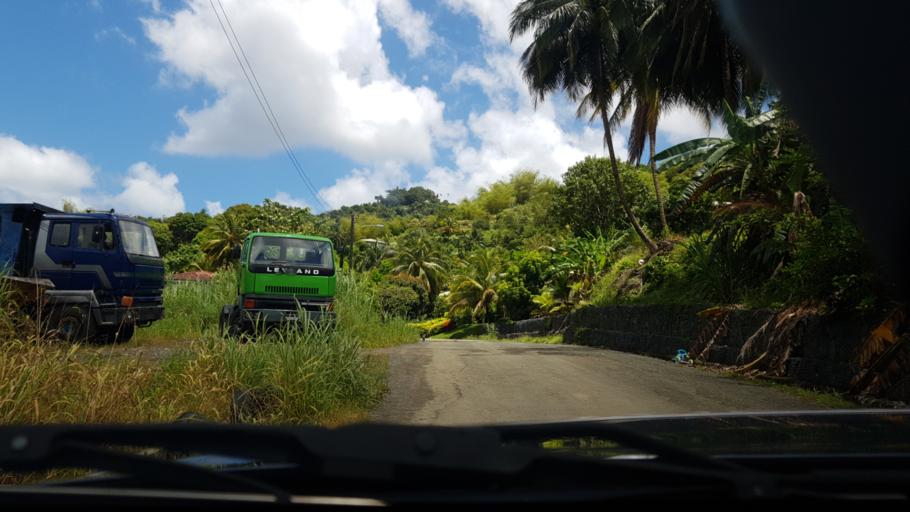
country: LC
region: Anse-la-Raye
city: Anse La Raye
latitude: 13.9517
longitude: -60.9961
